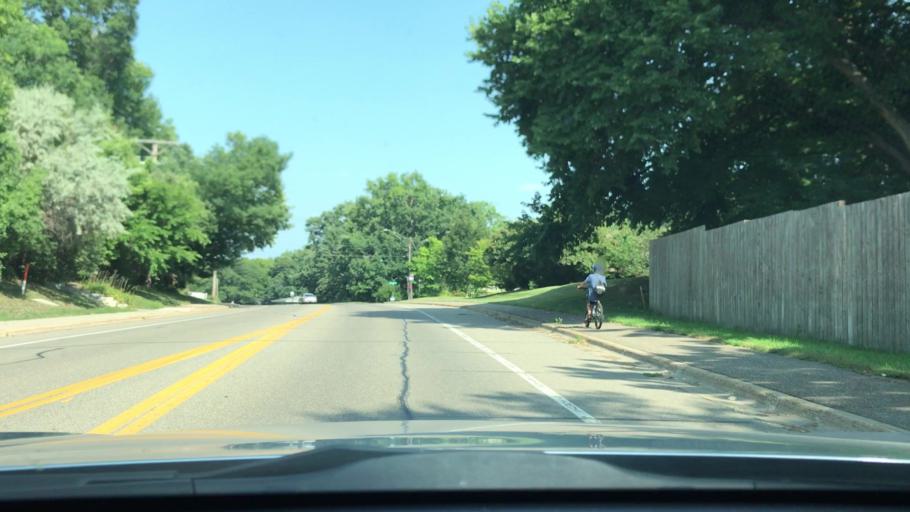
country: US
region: Minnesota
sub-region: Hennepin County
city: Edina
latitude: 44.9024
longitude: -93.3672
